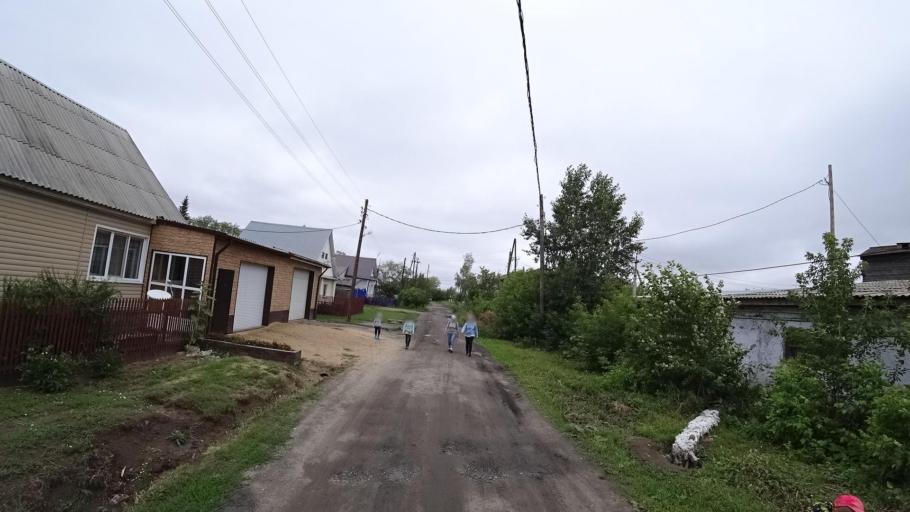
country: RU
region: Sverdlovsk
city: Kamyshlov
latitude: 56.8459
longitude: 62.7655
